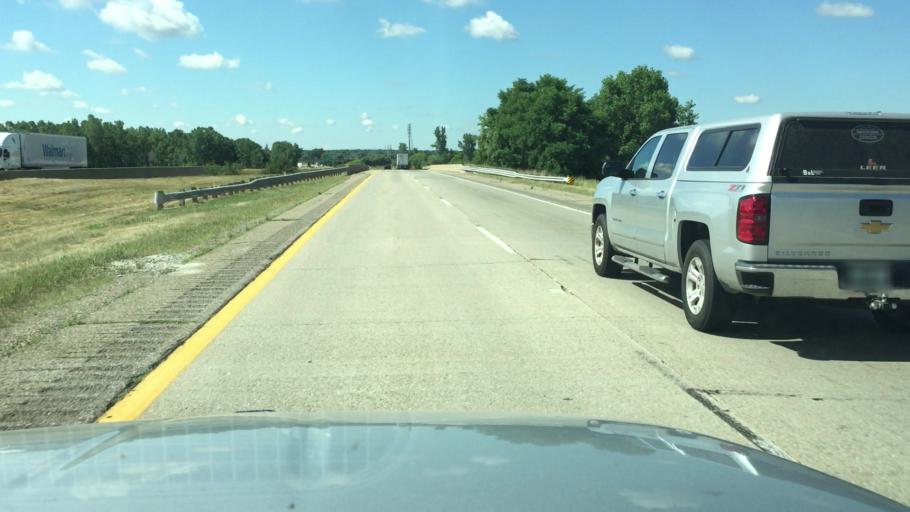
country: US
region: Michigan
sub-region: Eaton County
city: Charlotte
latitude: 42.5766
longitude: -84.8194
